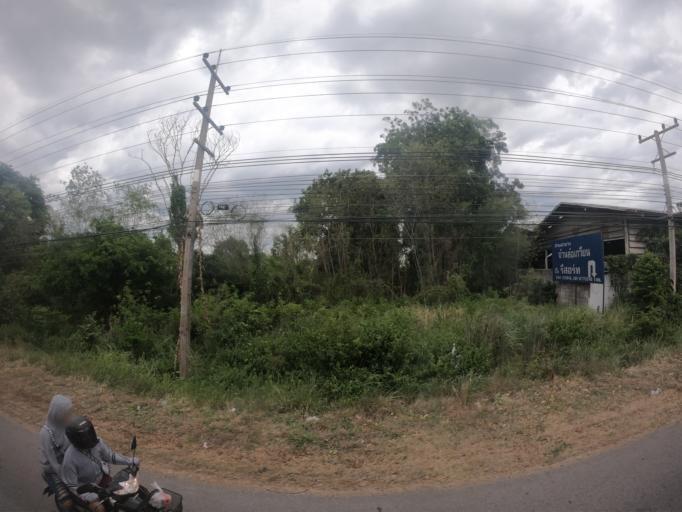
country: TH
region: Nakhon Ratchasima
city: Nakhon Ratchasima
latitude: 14.8842
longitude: 102.1713
